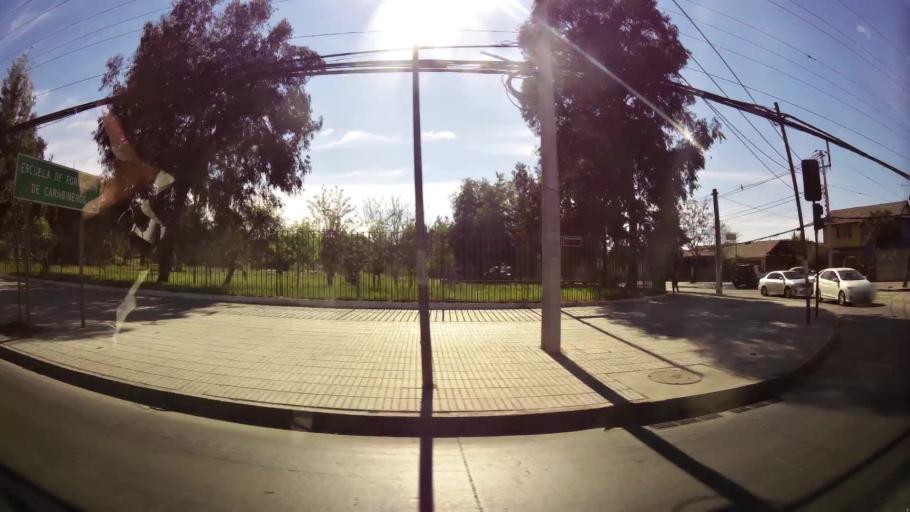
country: CL
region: Santiago Metropolitan
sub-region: Provincia de Santiago
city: Lo Prado
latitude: -33.4974
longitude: -70.7075
